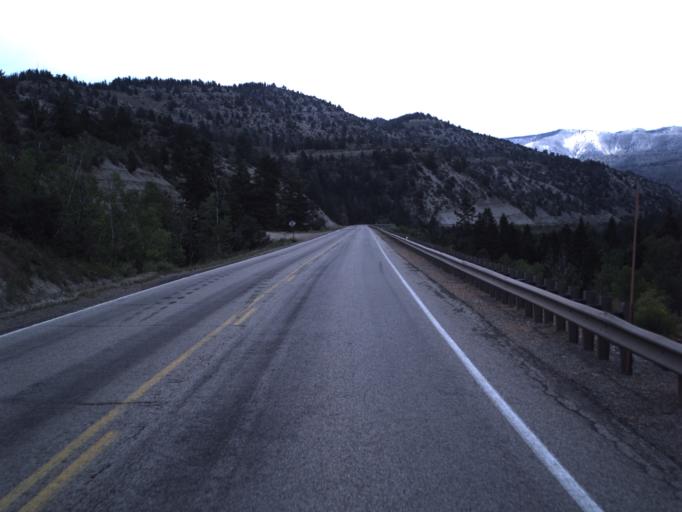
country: US
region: Utah
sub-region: Carbon County
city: Helper
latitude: 39.8986
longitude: -110.7480
